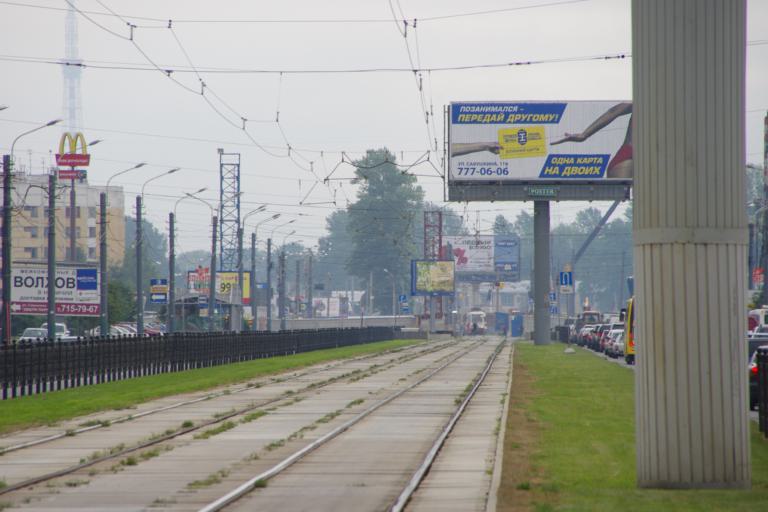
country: RU
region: Leningrad
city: Untolovo
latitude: 59.9872
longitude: 30.2151
